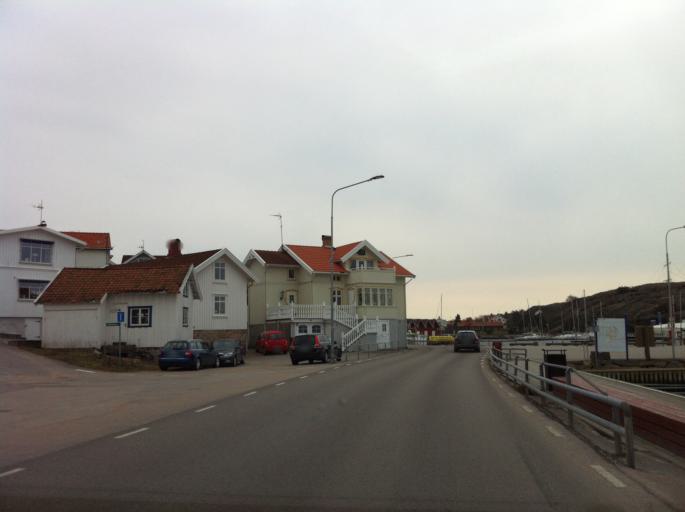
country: SE
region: Vaestra Goetaland
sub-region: Orust
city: Henan
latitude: 58.1599
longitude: 11.7060
